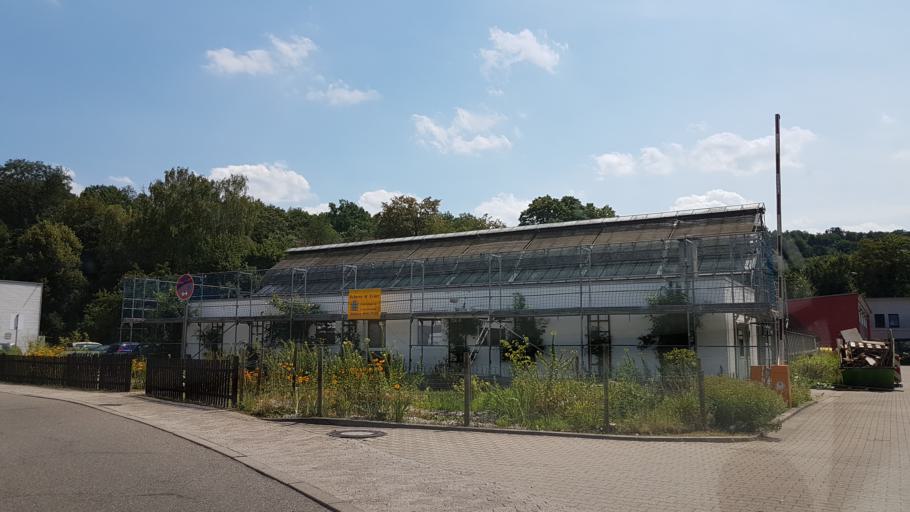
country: DE
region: Saarland
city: Homburg
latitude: 49.3043
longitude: 7.3395
